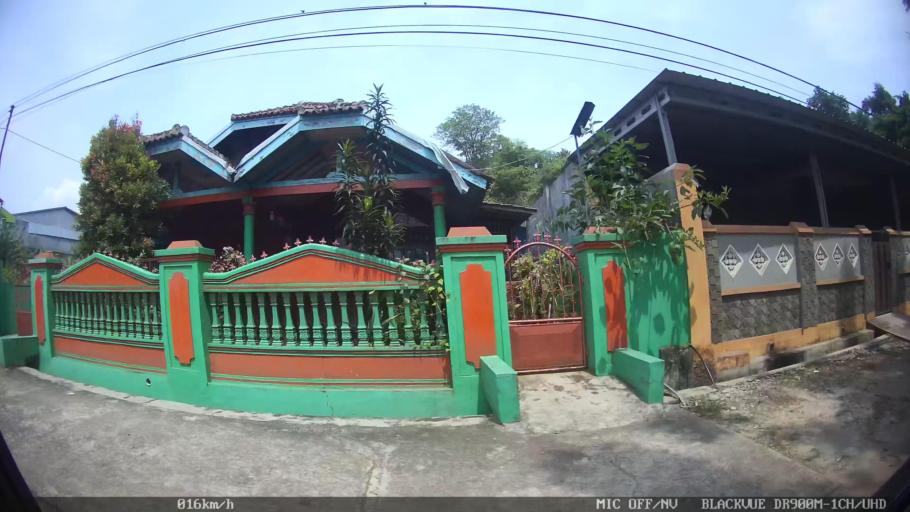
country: ID
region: Lampung
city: Bandarlampung
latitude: -5.4533
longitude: 105.2485
